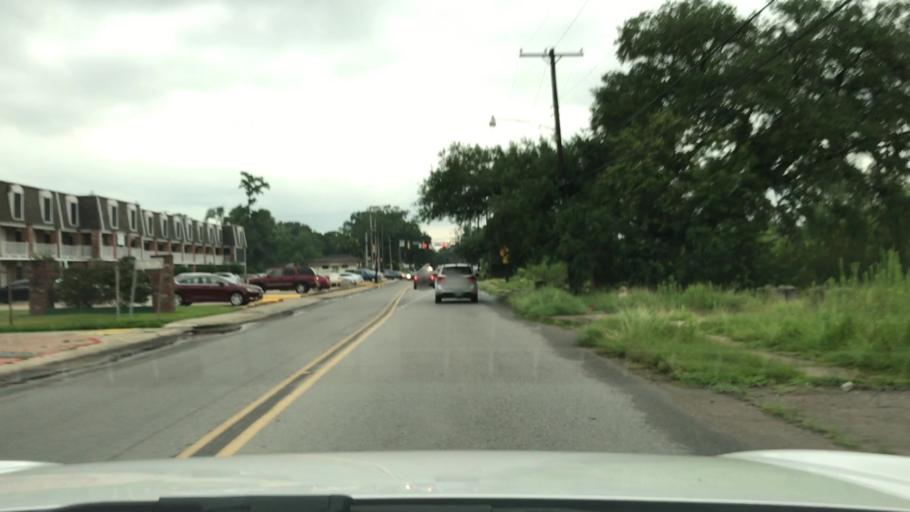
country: US
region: Louisiana
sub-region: East Baton Rouge Parish
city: Merrydale
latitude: 30.4784
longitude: -91.1175
